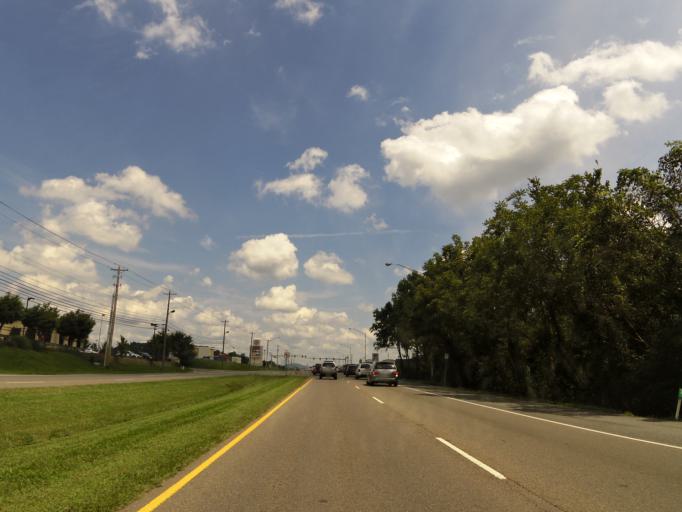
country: US
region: Tennessee
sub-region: Sullivan County
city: Bloomingdale
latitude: 36.5490
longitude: -82.4956
